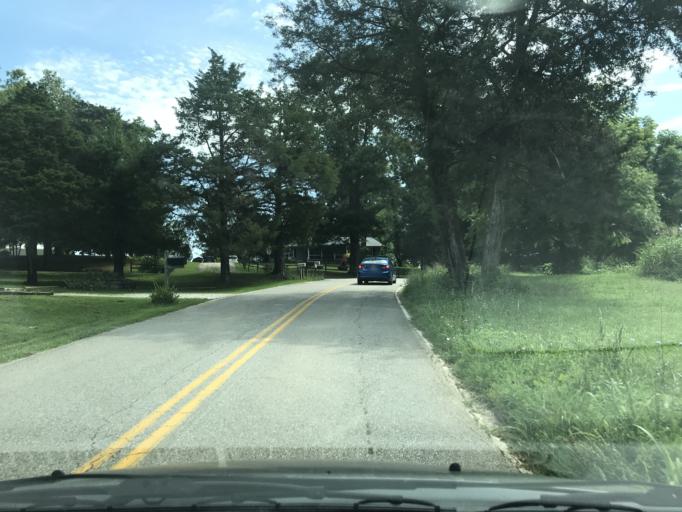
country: US
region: Tennessee
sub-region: Hamilton County
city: Lakesite
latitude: 35.1827
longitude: -85.0426
